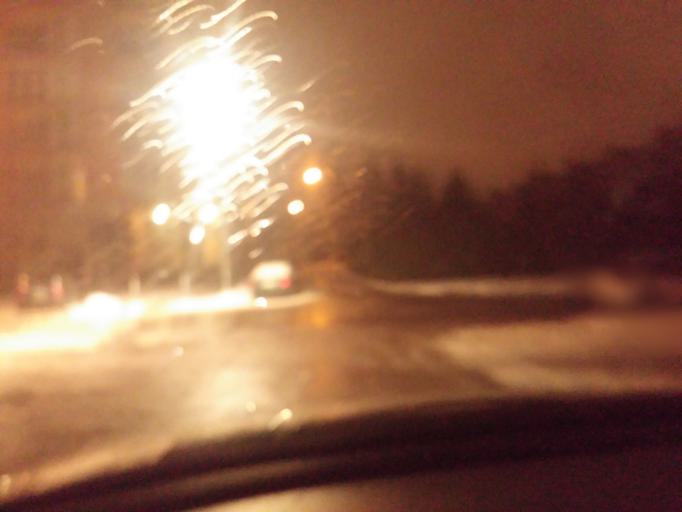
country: LT
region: Vilnius County
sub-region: Vilnius
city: Fabijoniskes
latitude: 54.7251
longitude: 25.2450
